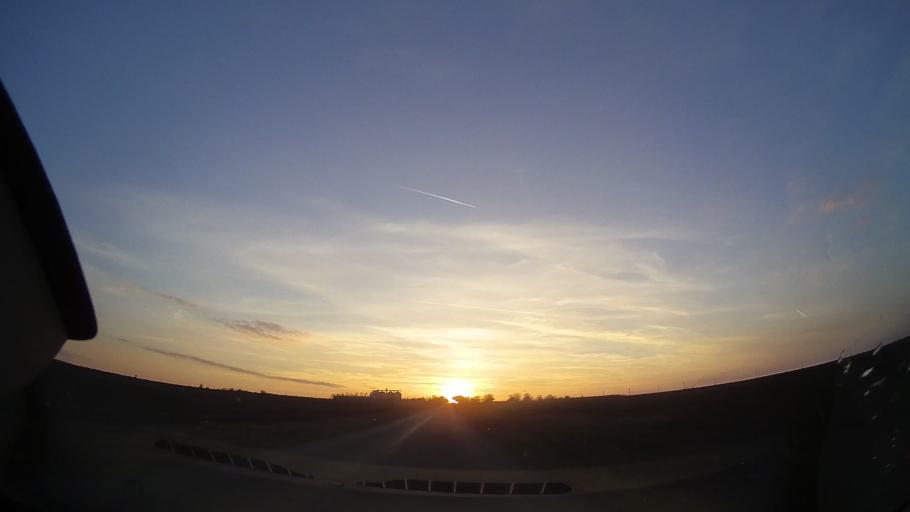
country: RO
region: Constanta
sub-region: Comuna Mereni
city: Mereni
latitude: 44.0233
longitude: 28.3578
